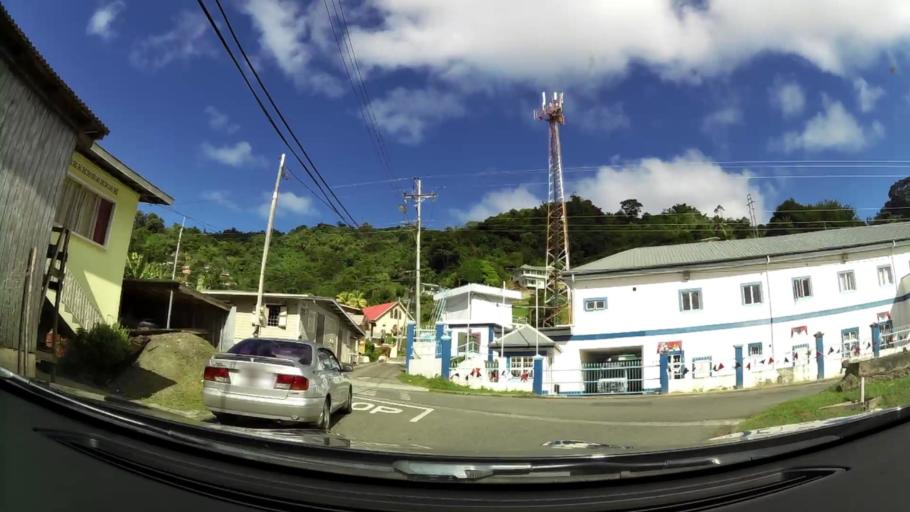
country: TT
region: Eastern Tobago
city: Roxborough
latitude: 11.3238
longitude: -60.5476
